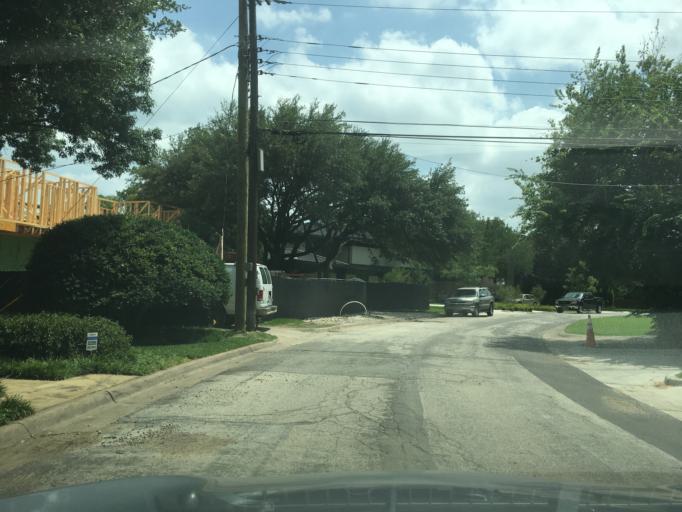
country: US
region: Texas
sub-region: Dallas County
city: Addison
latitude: 32.9054
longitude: -96.8230
